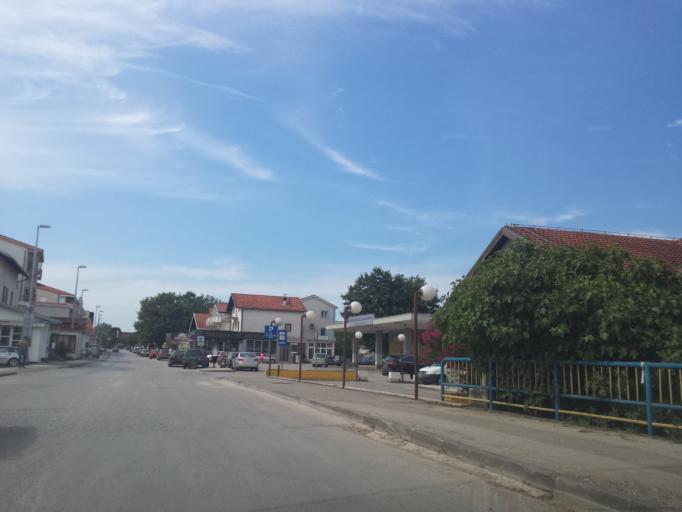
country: BA
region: Federation of Bosnia and Herzegovina
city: Citluk
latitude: 43.1950
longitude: 17.6791
